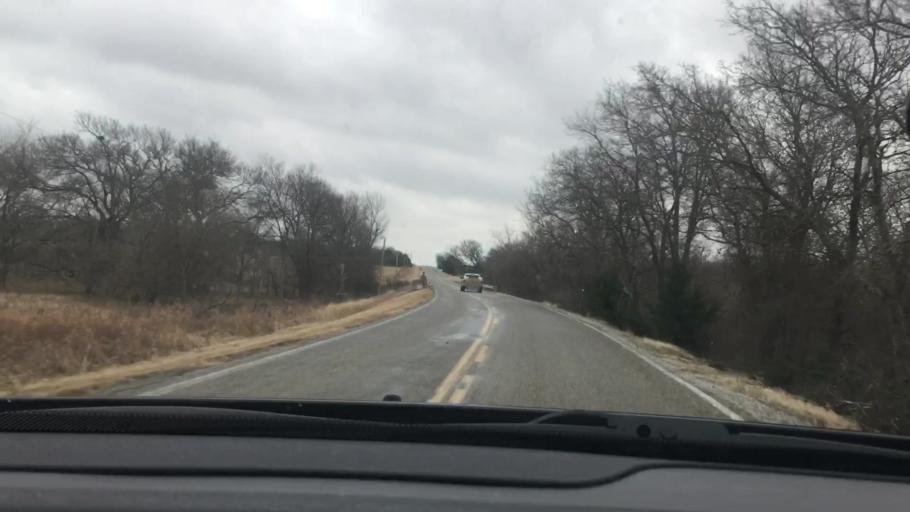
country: US
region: Oklahoma
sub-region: Johnston County
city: Tishomingo
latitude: 34.1434
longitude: -96.5456
